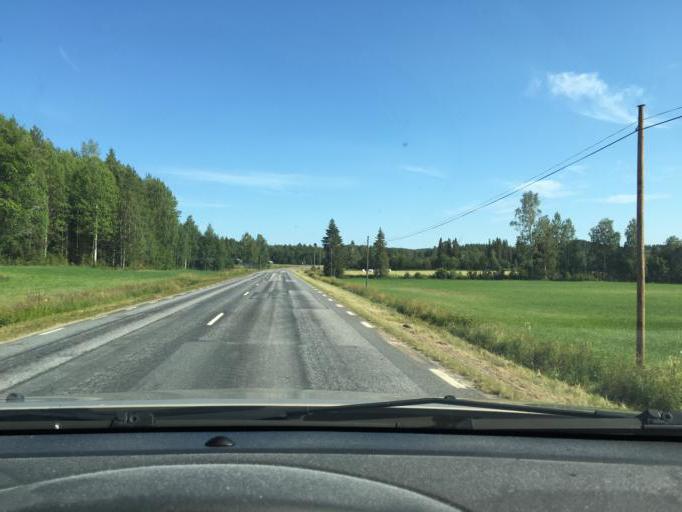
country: SE
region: Norrbotten
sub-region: Bodens Kommun
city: Boden
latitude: 65.9166
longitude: 21.8391
